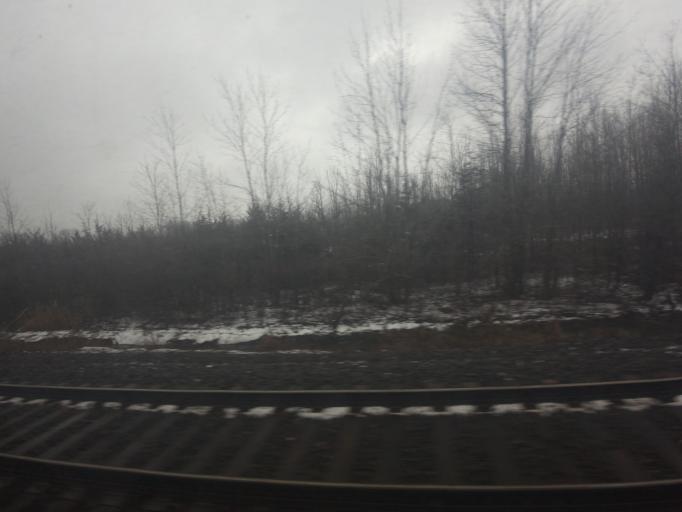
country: CA
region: Ontario
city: Belleville
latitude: 44.2039
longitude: -77.2763
